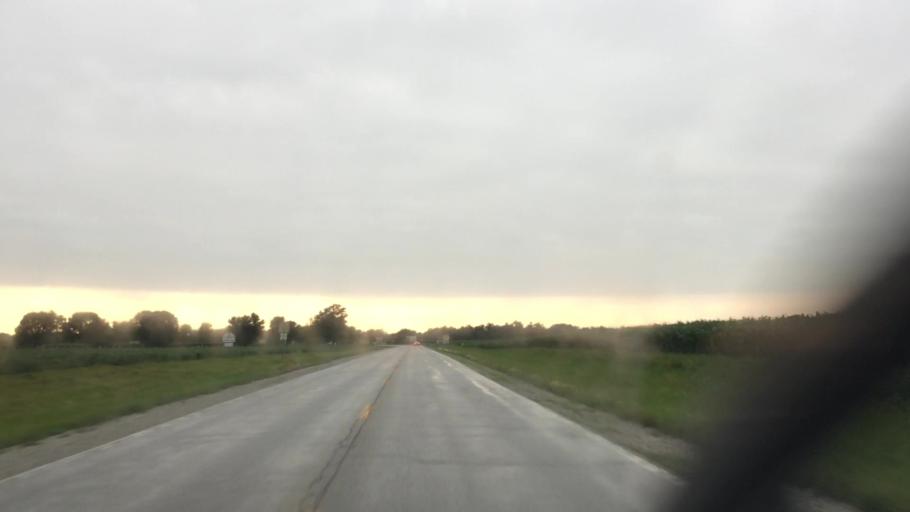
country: US
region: Illinois
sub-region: Hancock County
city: Nauvoo
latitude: 40.5523
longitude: -91.3565
